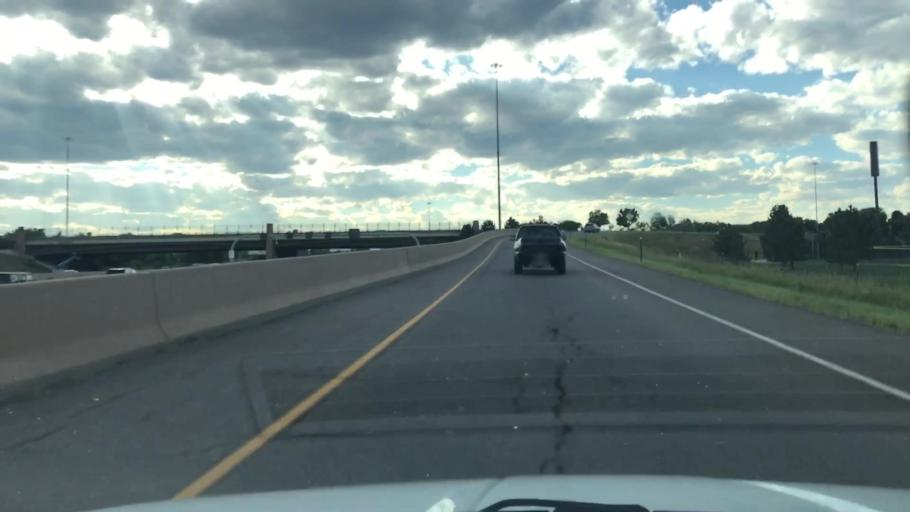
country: US
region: Colorado
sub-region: Adams County
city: Westminster
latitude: 39.8358
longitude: -105.0224
